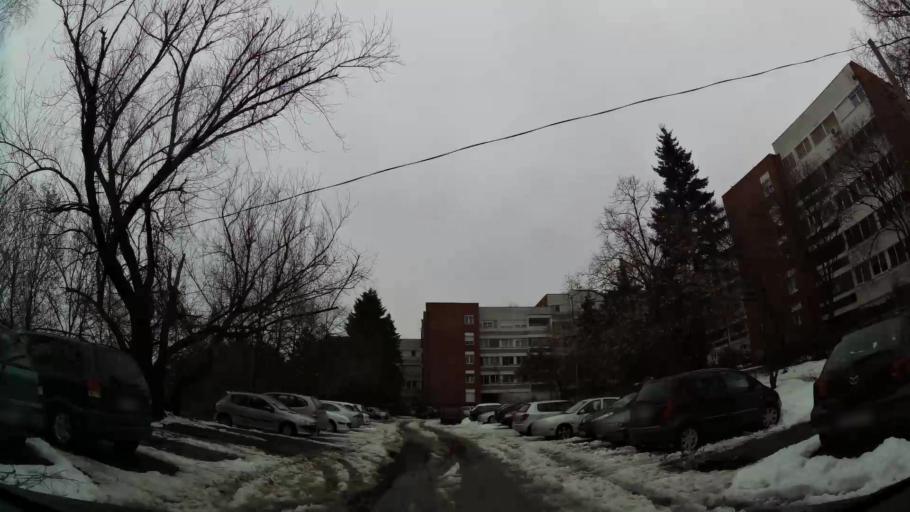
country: RS
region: Central Serbia
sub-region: Belgrade
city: Vozdovac
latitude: 44.7529
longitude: 20.5008
